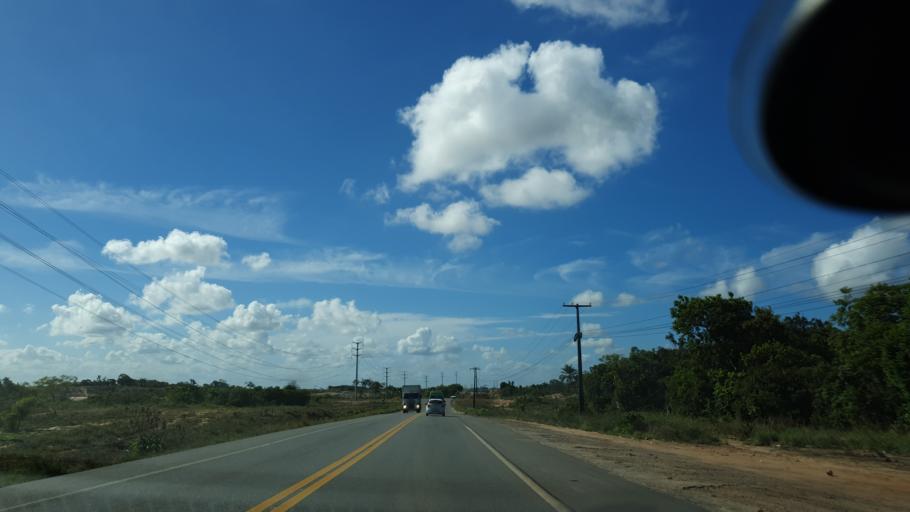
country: BR
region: Bahia
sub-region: Camacari
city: Camacari
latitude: -12.6995
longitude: -38.2177
